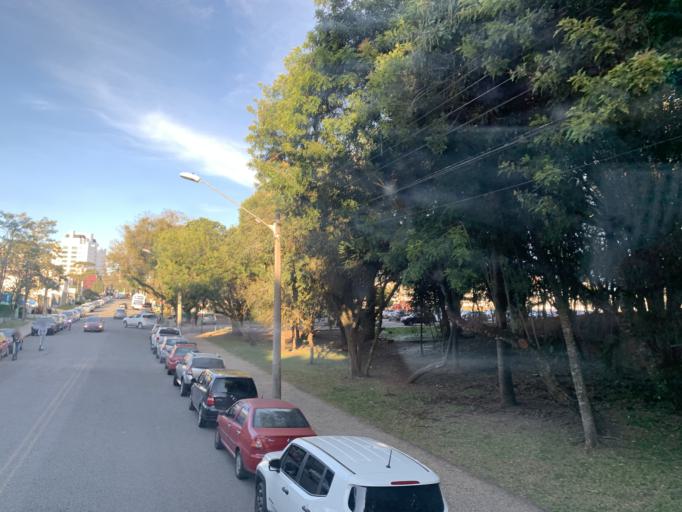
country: BR
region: Parana
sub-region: Curitiba
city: Curitiba
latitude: -25.4089
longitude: -49.2688
